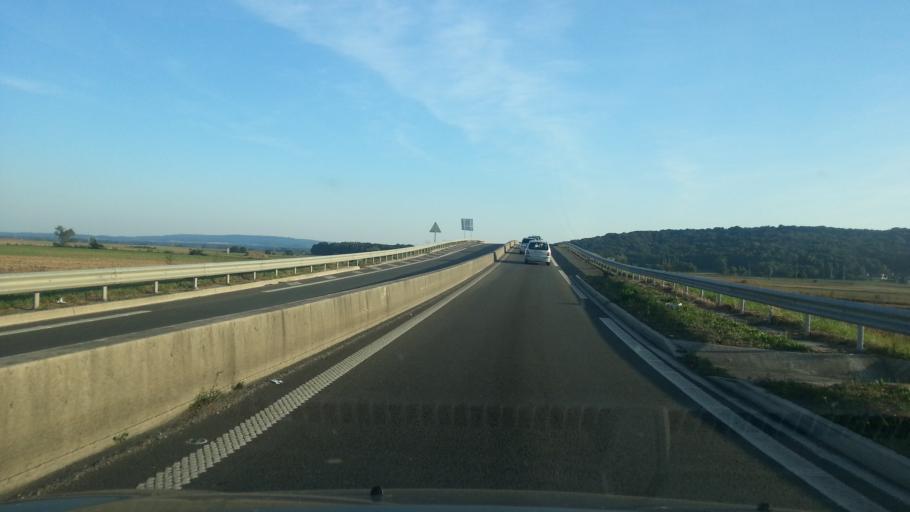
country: FR
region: Picardie
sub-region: Departement de l'Oise
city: Catenoy
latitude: 49.3787
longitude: 2.5233
